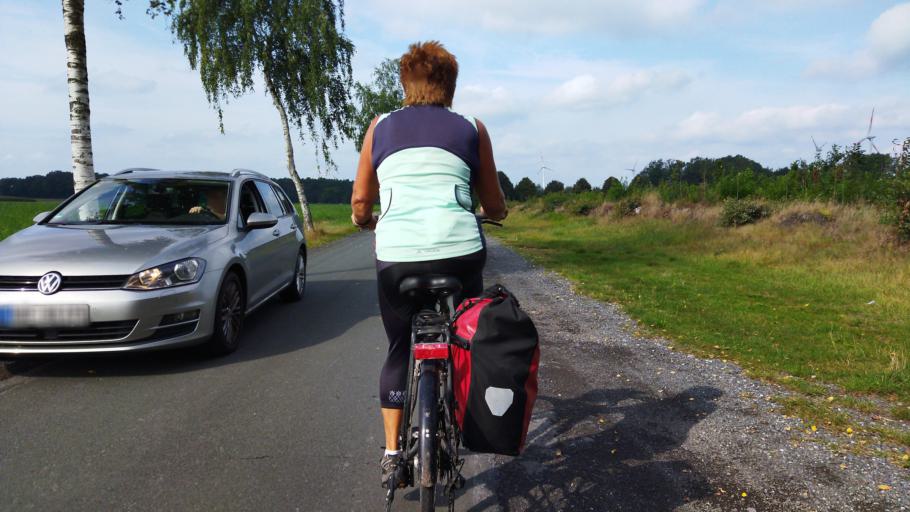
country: DE
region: North Rhine-Westphalia
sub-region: Regierungsbezirk Munster
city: Sassenberg
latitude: 52.0064
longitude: 8.0344
